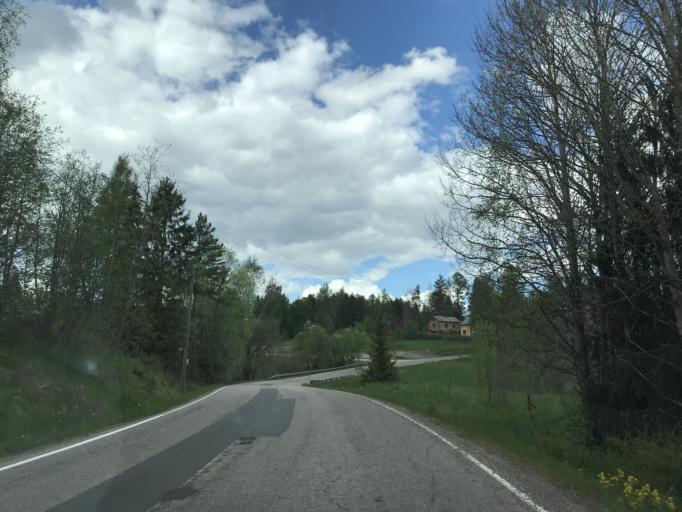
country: FI
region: Uusimaa
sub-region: Helsinki
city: Nurmijaervi
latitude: 60.4313
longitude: 24.7107
